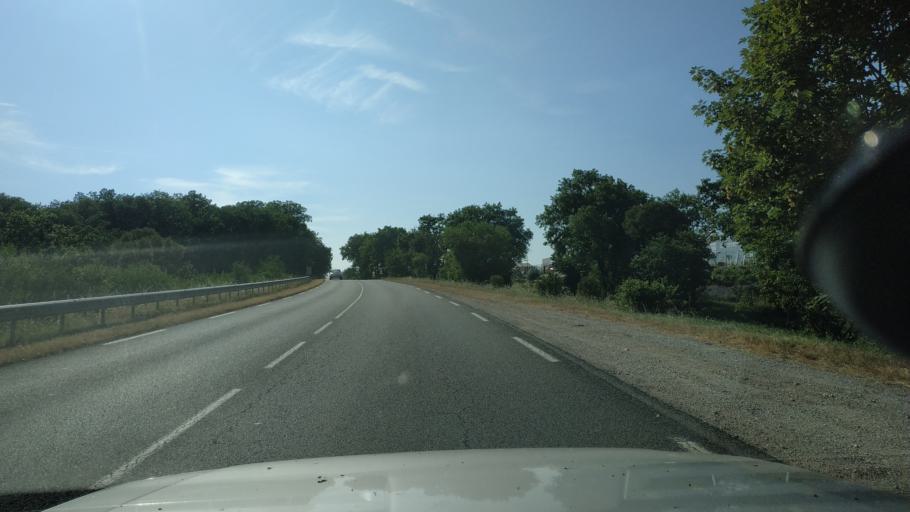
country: FR
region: Midi-Pyrenees
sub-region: Departement du Lot
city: Gramat
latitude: 44.7913
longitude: 1.7072
